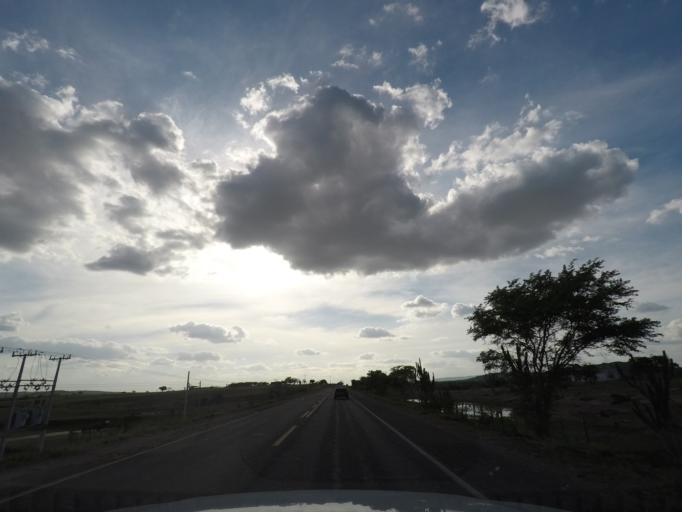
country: BR
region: Bahia
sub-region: Anguera
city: Anguera
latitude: -12.1865
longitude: -39.4853
